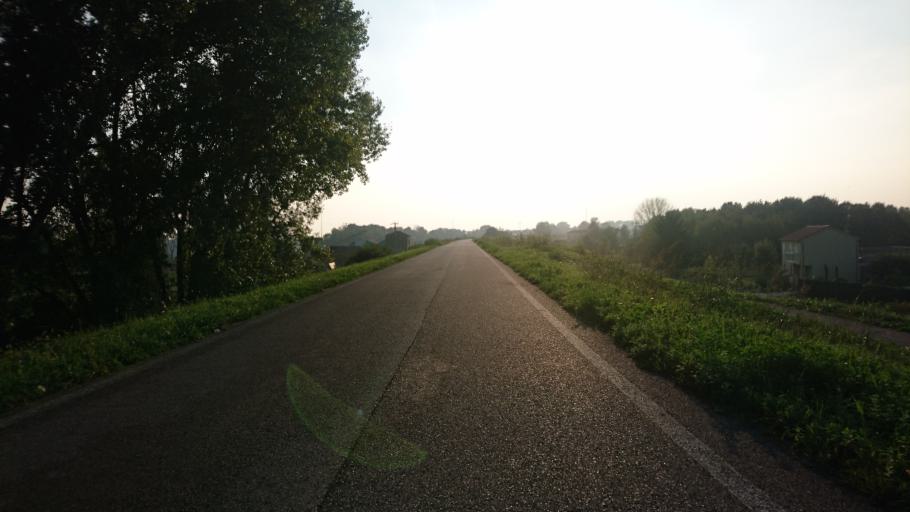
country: IT
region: Veneto
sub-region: Provincia di Rovigo
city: Santa Maria Maddalena
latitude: 44.8936
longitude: 11.6262
